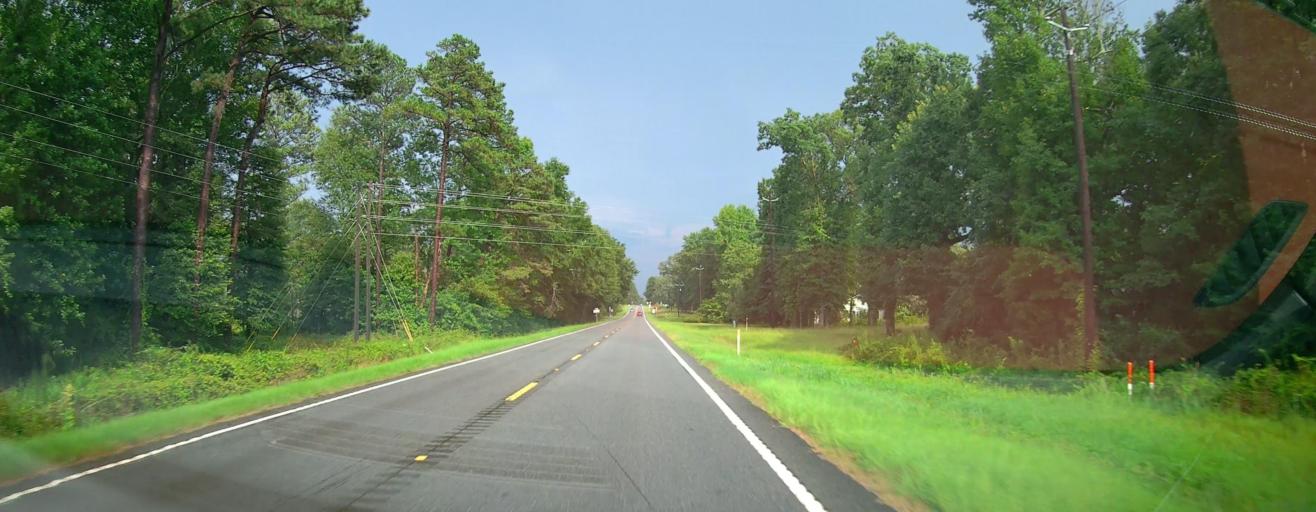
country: US
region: Georgia
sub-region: Twiggs County
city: Jeffersonville
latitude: 32.6060
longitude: -83.2581
